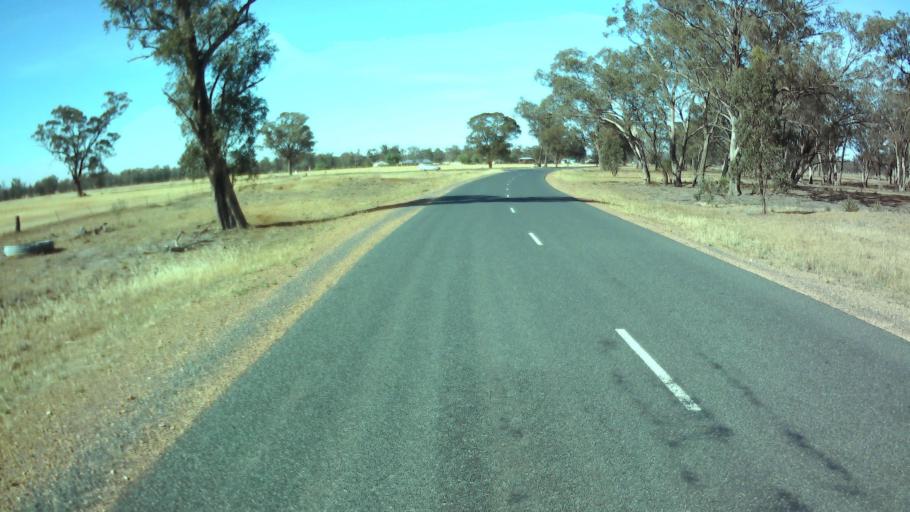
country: AU
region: New South Wales
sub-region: Weddin
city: Grenfell
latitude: -34.0955
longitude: 147.8858
